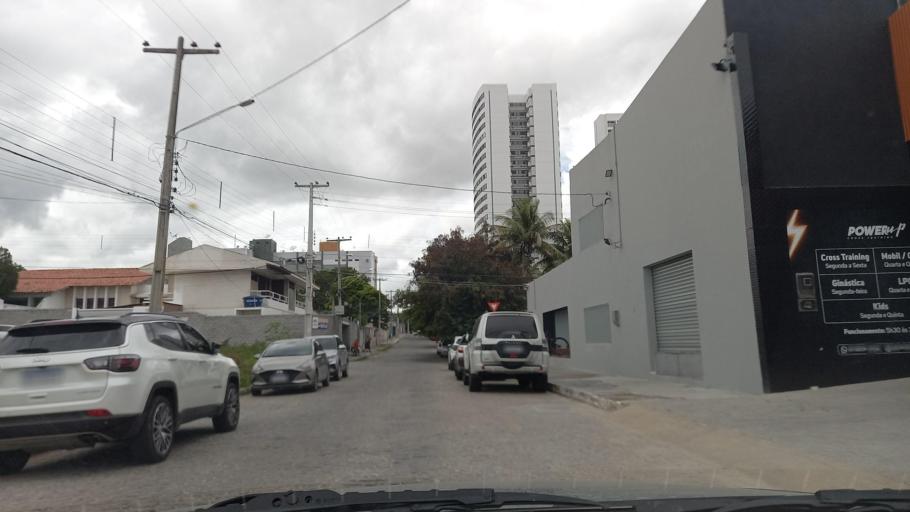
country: BR
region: Pernambuco
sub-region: Caruaru
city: Caruaru
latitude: -8.2724
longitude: -35.9676
